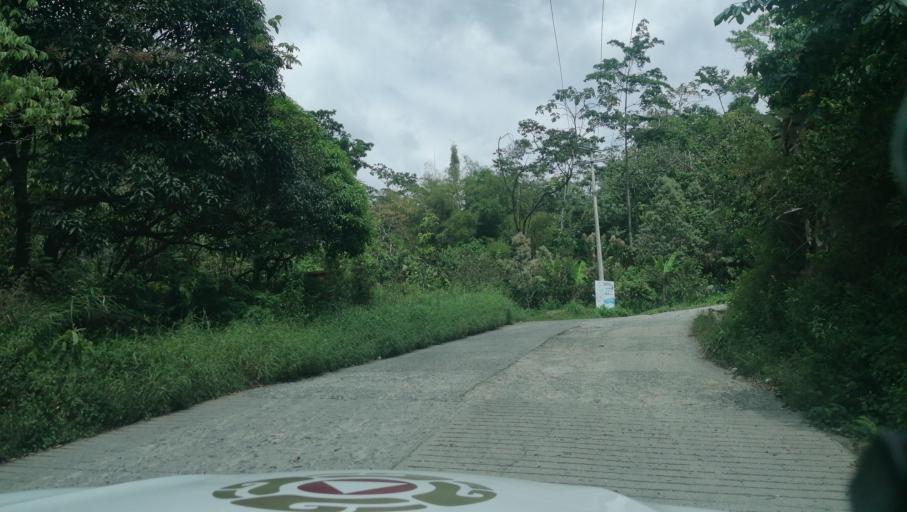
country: MX
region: Chiapas
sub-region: Cacahoatan
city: Benito Juarez
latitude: 15.1110
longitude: -92.2102
